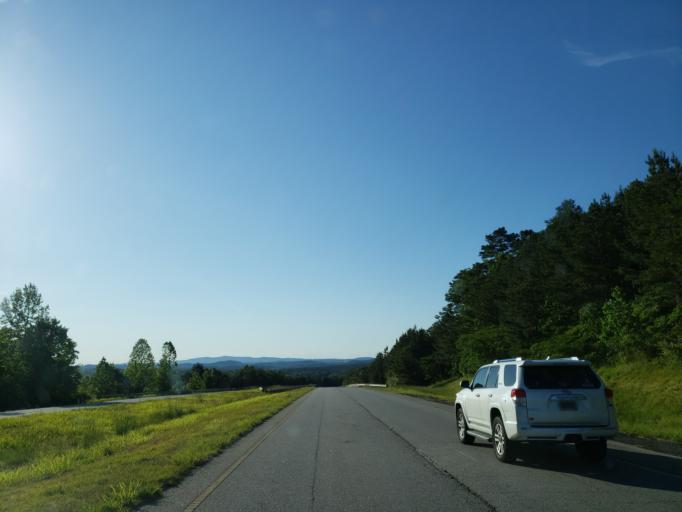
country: US
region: Georgia
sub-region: Haralson County
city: Buchanan
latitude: 33.9103
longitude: -85.2409
